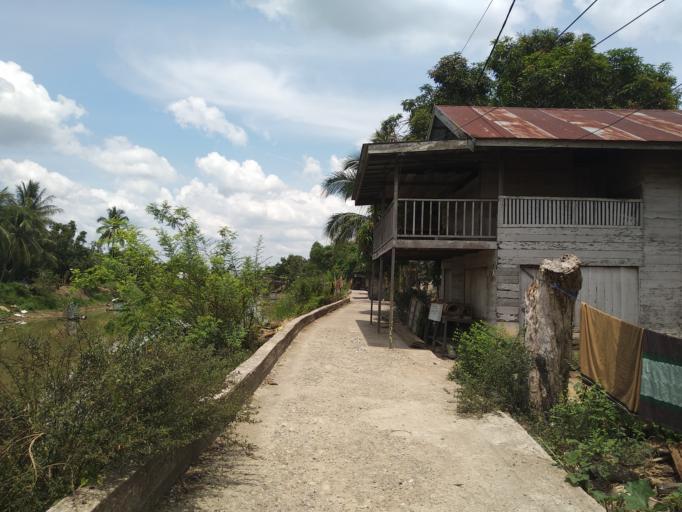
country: ID
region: South Kalimantan
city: Amuntai
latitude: -2.3857
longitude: 115.2335
